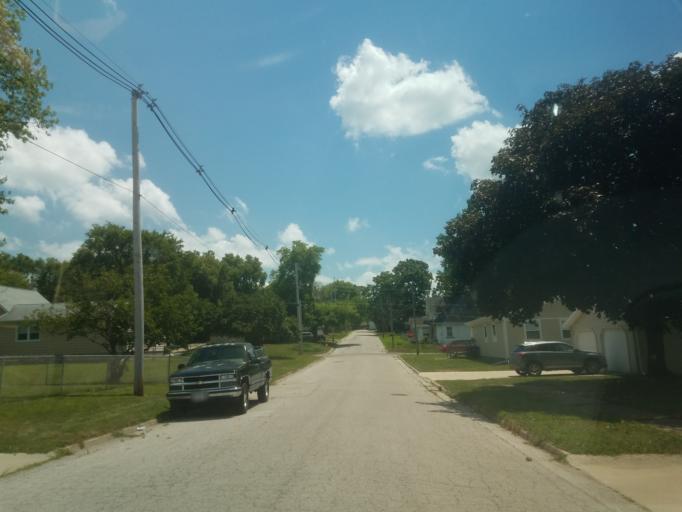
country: US
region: Illinois
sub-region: McLean County
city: Bloomington
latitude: 40.4716
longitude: -89.0119
